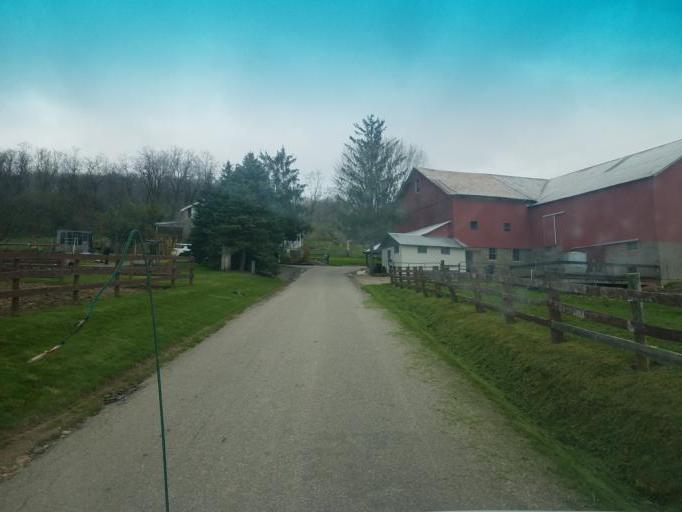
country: US
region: Ohio
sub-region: Stark County
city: Beach City
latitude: 40.6204
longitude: -81.6577
